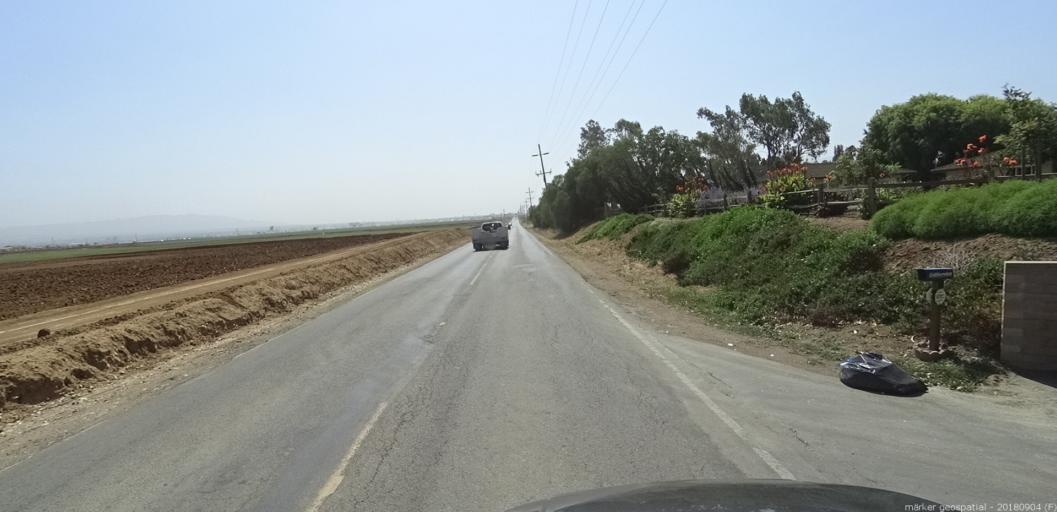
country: US
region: California
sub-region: Monterey County
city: Gonzales
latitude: 36.5483
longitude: -121.4716
